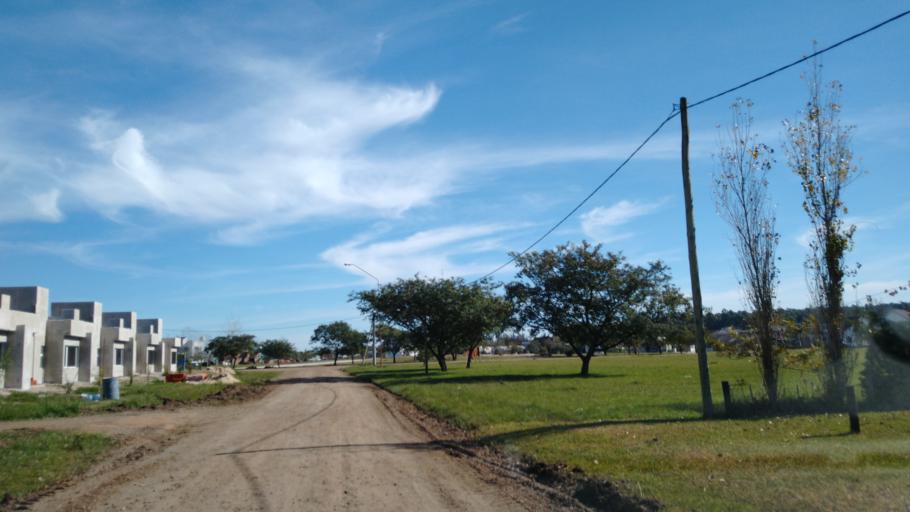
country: AR
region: Entre Rios
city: Chajari
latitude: -30.7431
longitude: -58.0103
